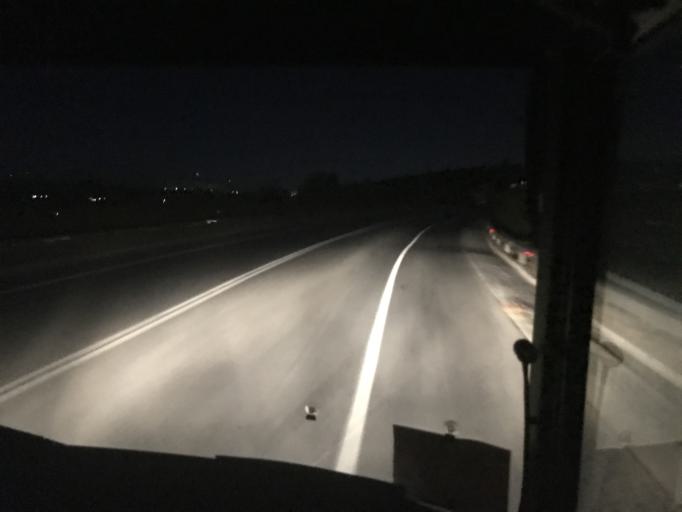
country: GR
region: Crete
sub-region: Nomos Irakleiou
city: Skalanion
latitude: 35.2737
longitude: 25.1836
